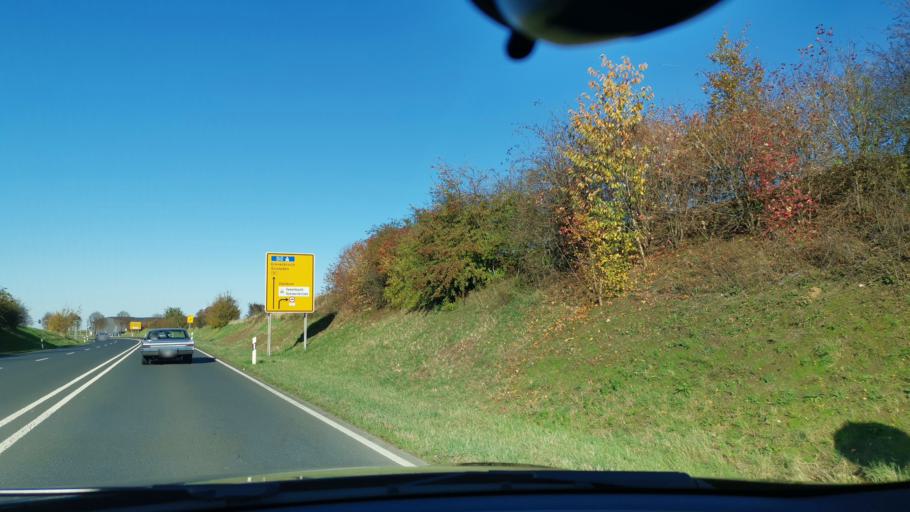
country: DE
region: North Rhine-Westphalia
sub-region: Regierungsbezirk Dusseldorf
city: Rommerskirchen
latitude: 51.0349
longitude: 6.6747
